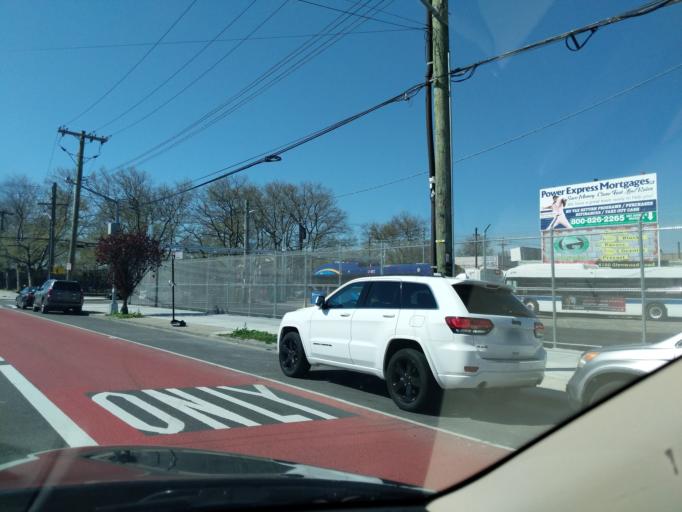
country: US
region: New York
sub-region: Kings County
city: Brooklyn
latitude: 40.6195
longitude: -73.9270
